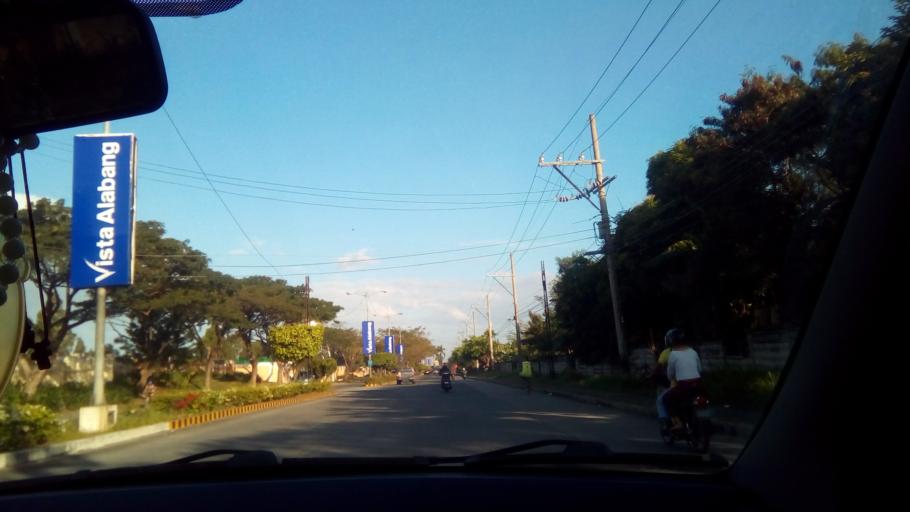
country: PH
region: Calabarzon
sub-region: Province of Laguna
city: San Pedro
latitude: 14.3818
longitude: 121.0128
